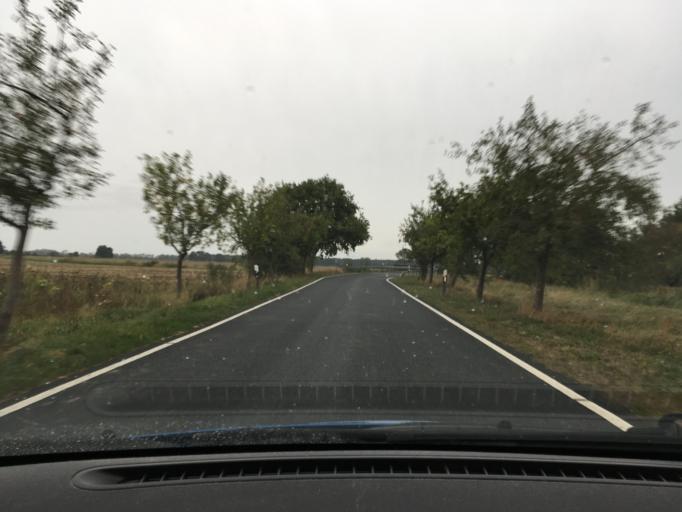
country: DE
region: Lower Saxony
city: Hitzacker
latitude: 53.1899
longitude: 11.0372
